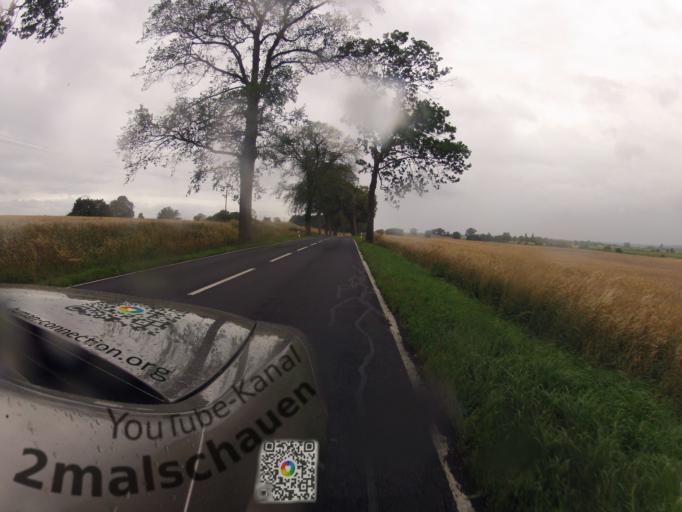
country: DE
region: Mecklenburg-Vorpommern
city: Seebad Heringsdorf
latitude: 53.8867
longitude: 14.1161
